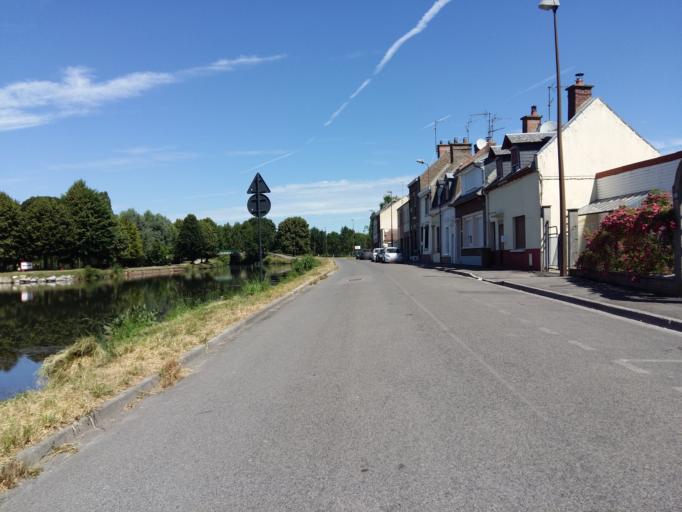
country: FR
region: Picardie
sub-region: Departement de la Somme
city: Amiens
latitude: 49.9075
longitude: 2.2821
